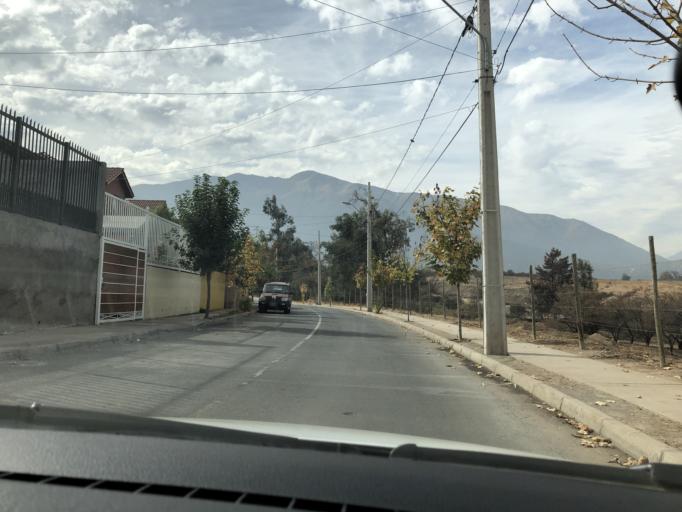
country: CL
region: Santiago Metropolitan
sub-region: Provincia de Cordillera
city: Puente Alto
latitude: -33.5890
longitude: -70.5309
